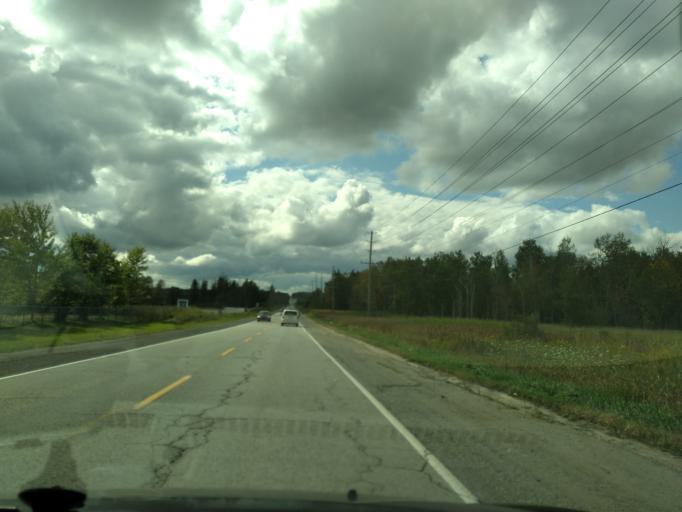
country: CA
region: Ontario
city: Innisfil
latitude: 44.2969
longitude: -79.6272
